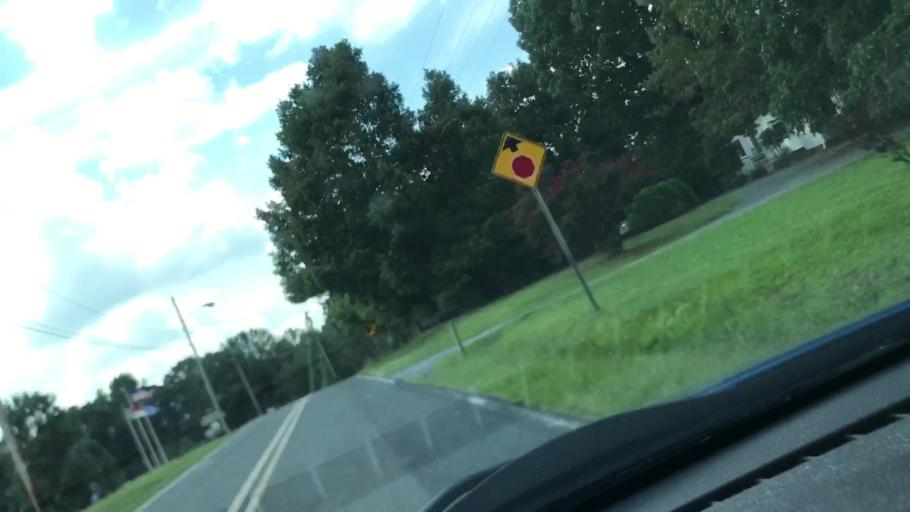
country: US
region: North Carolina
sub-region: Randolph County
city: Randleman
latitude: 35.8018
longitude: -79.8161
